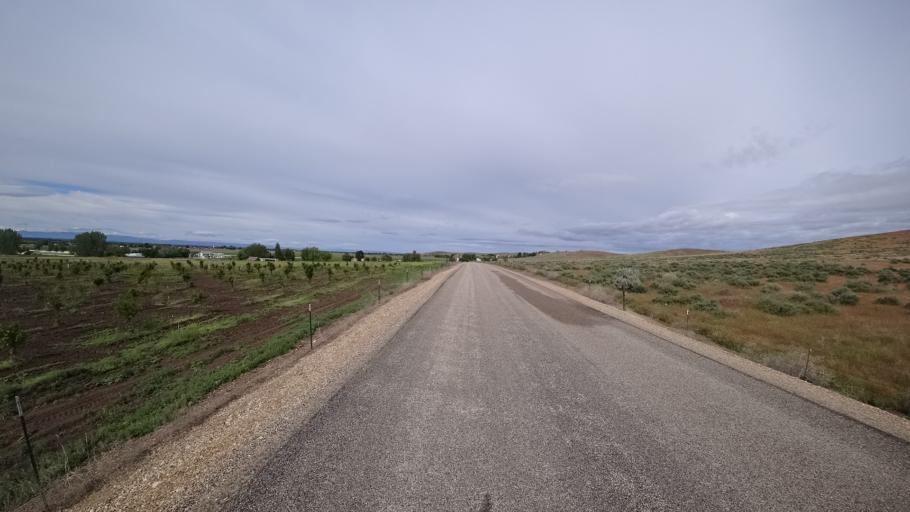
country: US
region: Idaho
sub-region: Ada County
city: Eagle
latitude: 43.7354
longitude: -116.4077
